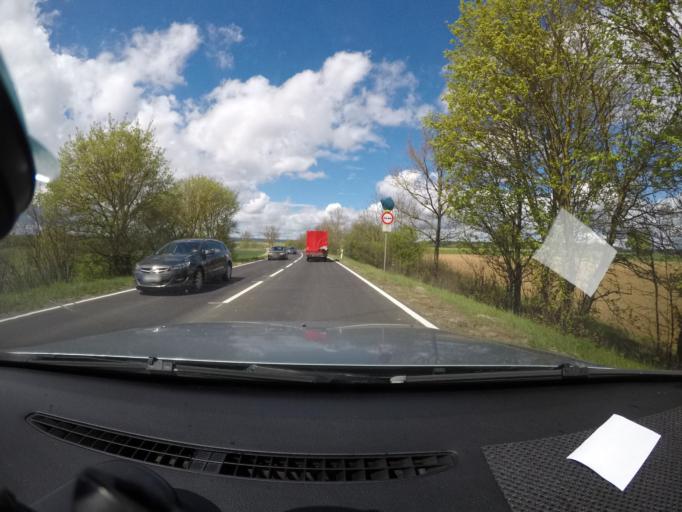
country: DE
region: Baden-Wuerttemberg
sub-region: Freiburg Region
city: Villingen-Schwenningen
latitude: 48.0762
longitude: 8.4969
